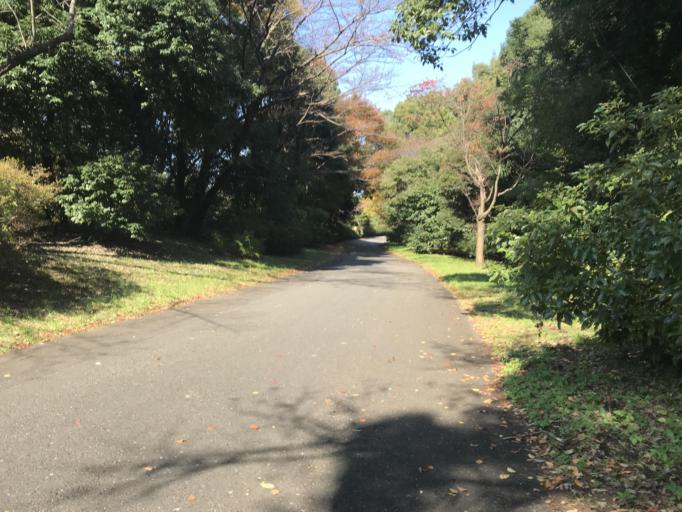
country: JP
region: Tokyo
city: Hino
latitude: 35.7076
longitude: 139.3990
